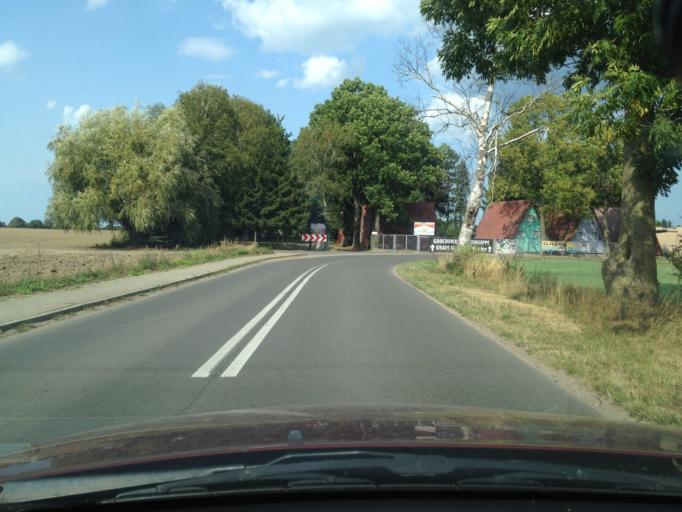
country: PL
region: West Pomeranian Voivodeship
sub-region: Powiat gryficki
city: Pobierowo
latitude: 54.0185
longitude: 14.8693
